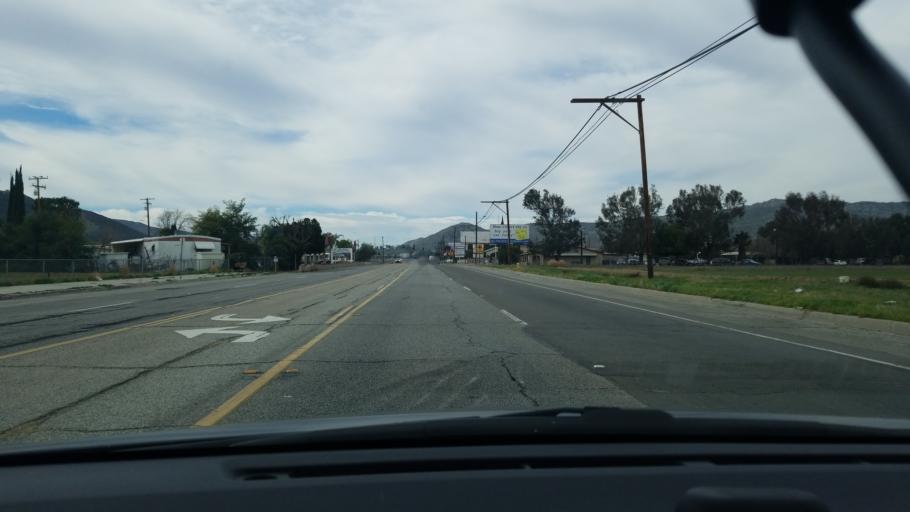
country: US
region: California
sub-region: Riverside County
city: Green Acres
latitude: 33.7439
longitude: -117.0467
